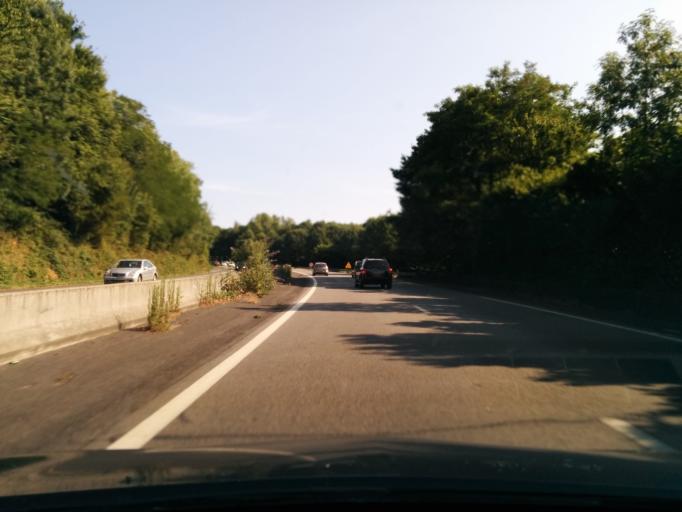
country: FR
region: Limousin
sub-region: Departement de la Haute-Vienne
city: Condat-sur-Vienne
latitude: 45.7992
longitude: 1.2960
